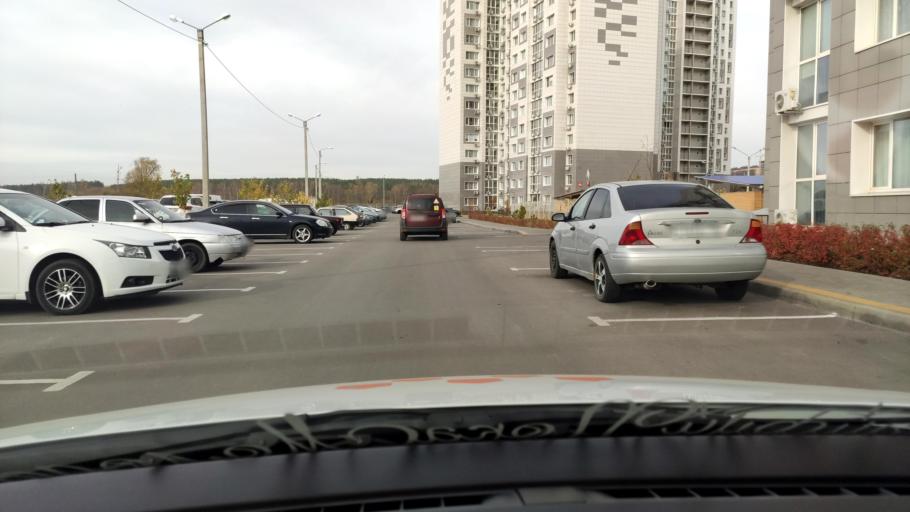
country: RU
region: Voronezj
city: Voronezh
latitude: 51.6726
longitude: 39.1344
